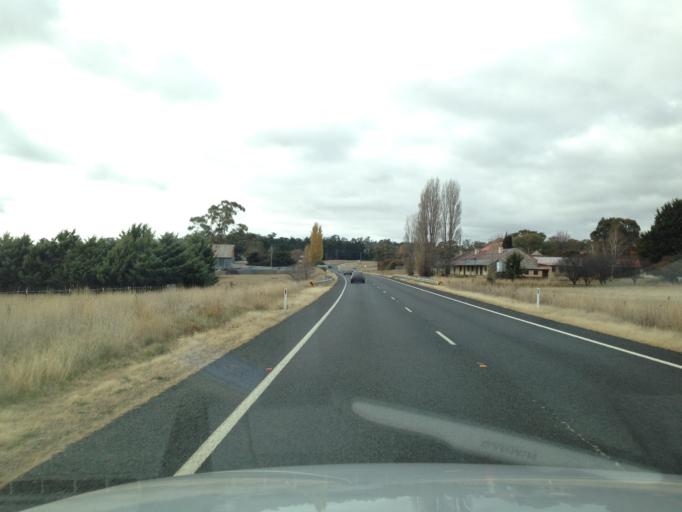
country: AU
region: New South Wales
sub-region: Cooma-Monaro
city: Cooma
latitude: -36.2433
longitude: 149.0609
